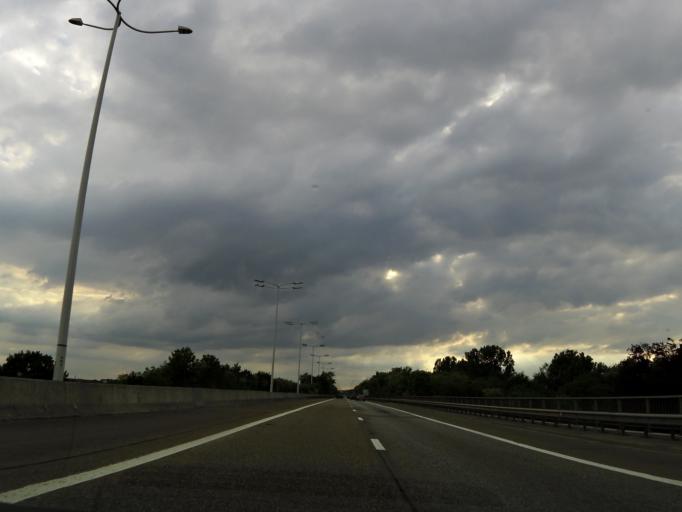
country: BE
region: Flanders
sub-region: Provincie Limburg
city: Maasmechelen
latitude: 50.9522
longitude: 5.7106
